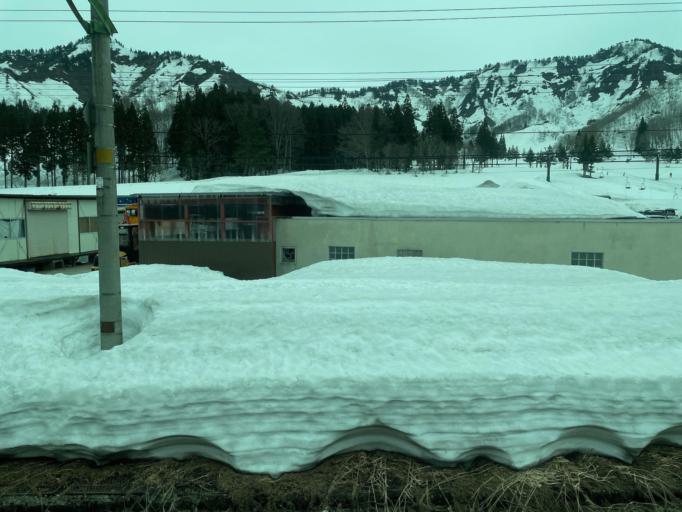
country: JP
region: Niigata
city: Shiozawa
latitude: 36.9140
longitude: 138.8485
